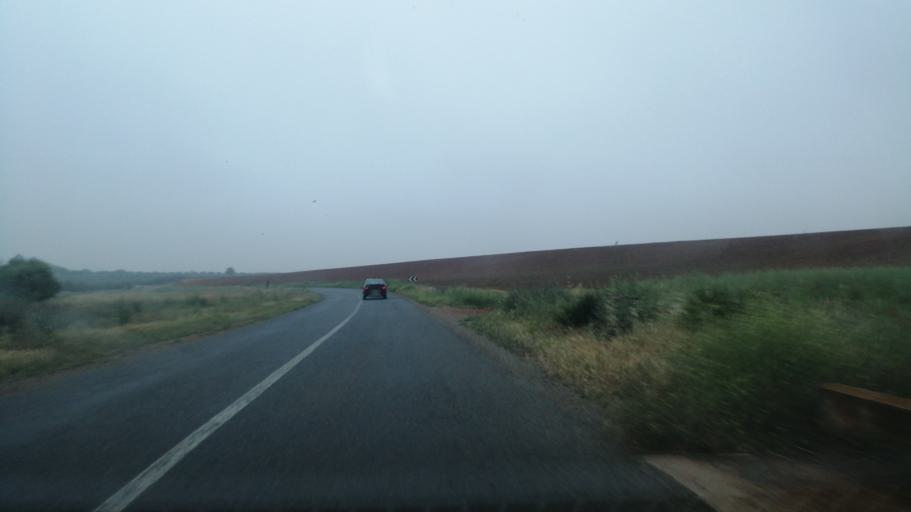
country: MA
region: Rabat-Sale-Zemmour-Zaer
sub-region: Khemisset
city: Tiflet
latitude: 33.7549
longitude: -6.2673
